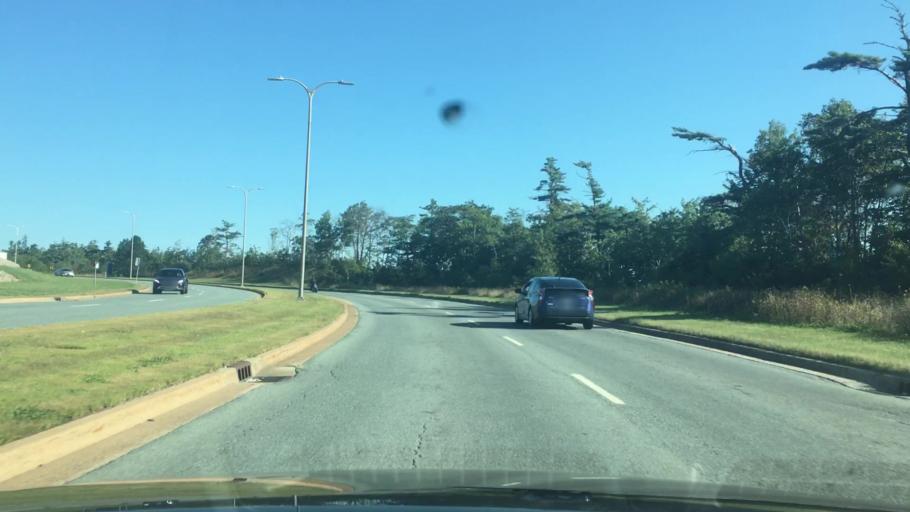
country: CA
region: Nova Scotia
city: Dartmouth
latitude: 44.7187
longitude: -63.5806
